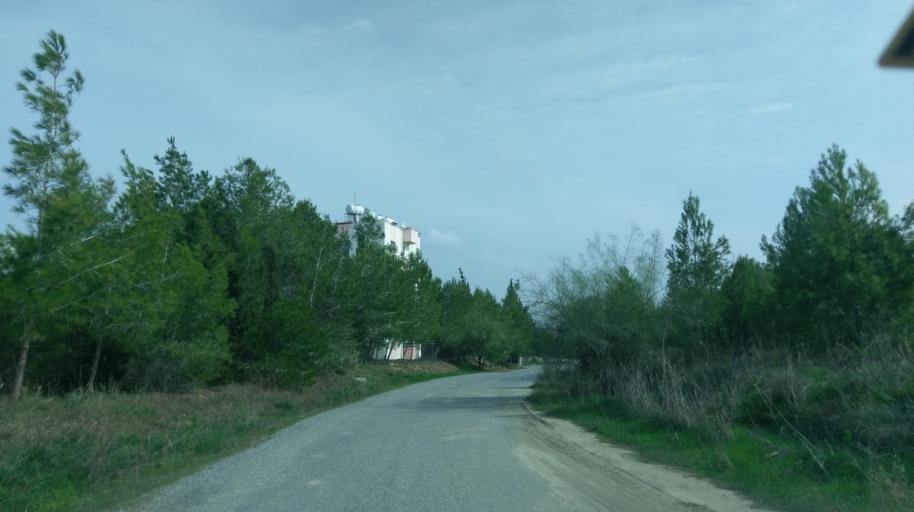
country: CY
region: Keryneia
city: Lapithos
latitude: 35.2662
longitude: 33.1256
